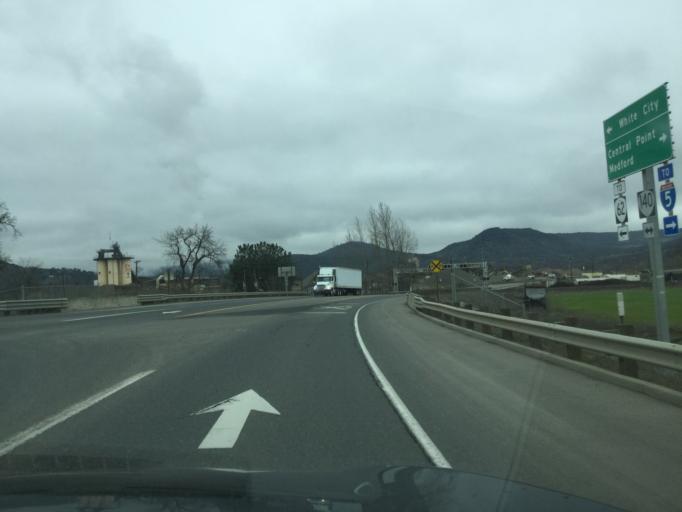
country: US
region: Oregon
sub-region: Jackson County
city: Central Point
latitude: 42.4205
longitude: -122.9572
